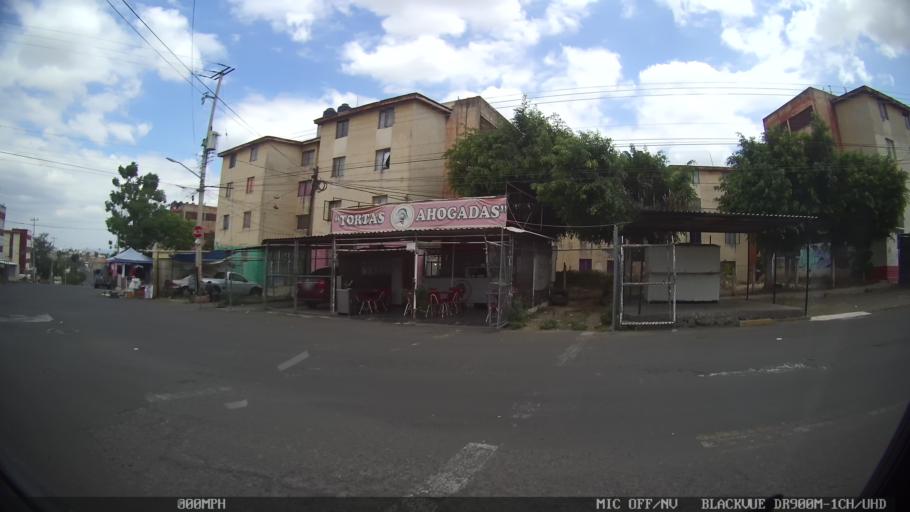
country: MX
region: Jalisco
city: Tonala
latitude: 20.6317
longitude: -103.2554
